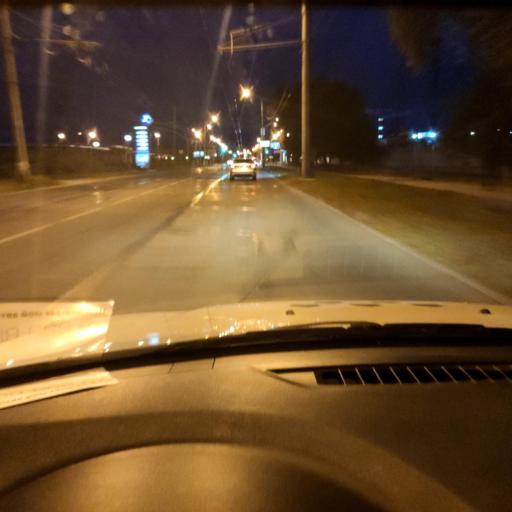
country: RU
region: Samara
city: Tol'yatti
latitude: 53.5312
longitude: 49.4383
